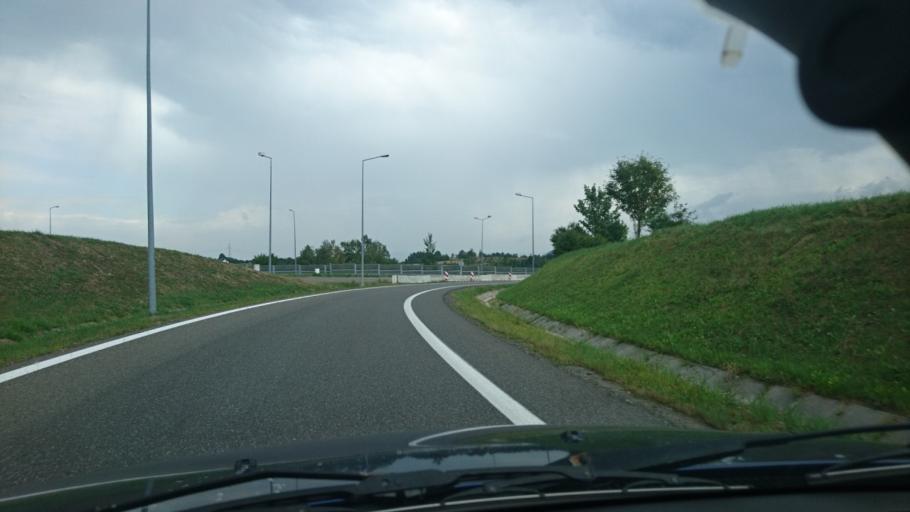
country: PL
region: Silesian Voivodeship
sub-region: Powiat zywiecki
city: Radziechowy
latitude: 49.6276
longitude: 19.1386
